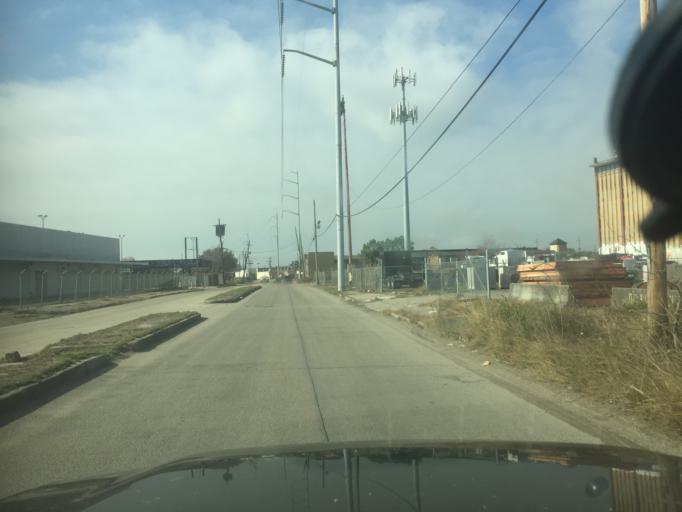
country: US
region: Louisiana
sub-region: Saint Bernard Parish
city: Arabi
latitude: 30.0060
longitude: -90.0298
